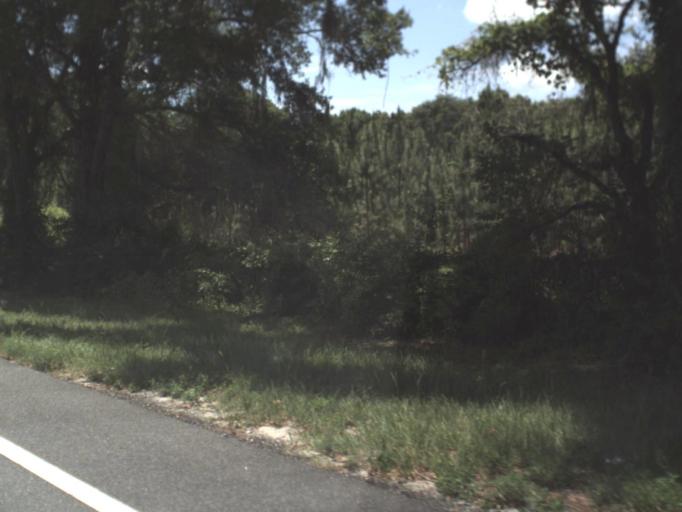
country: US
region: Florida
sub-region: Lafayette County
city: Mayo
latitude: 29.8706
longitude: -82.9575
